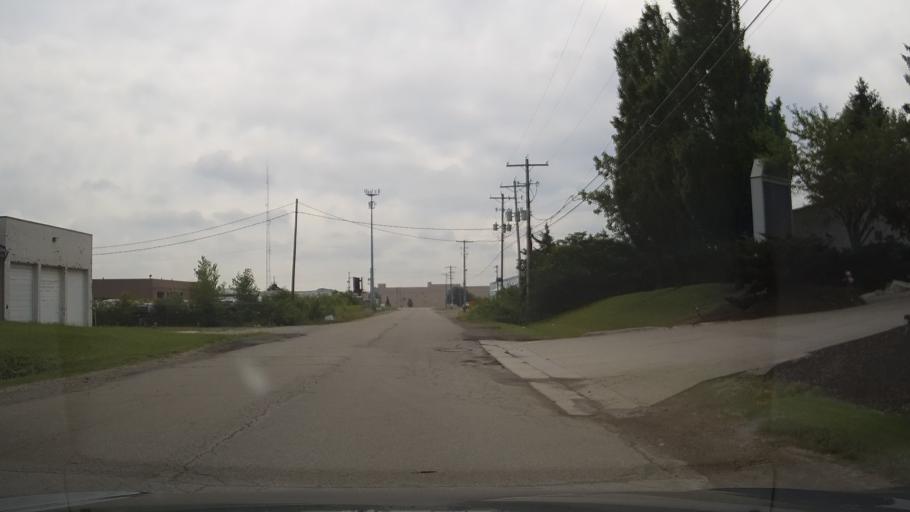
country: US
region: Ohio
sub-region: Franklin County
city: Lincoln Village
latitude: 39.9605
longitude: -83.1147
